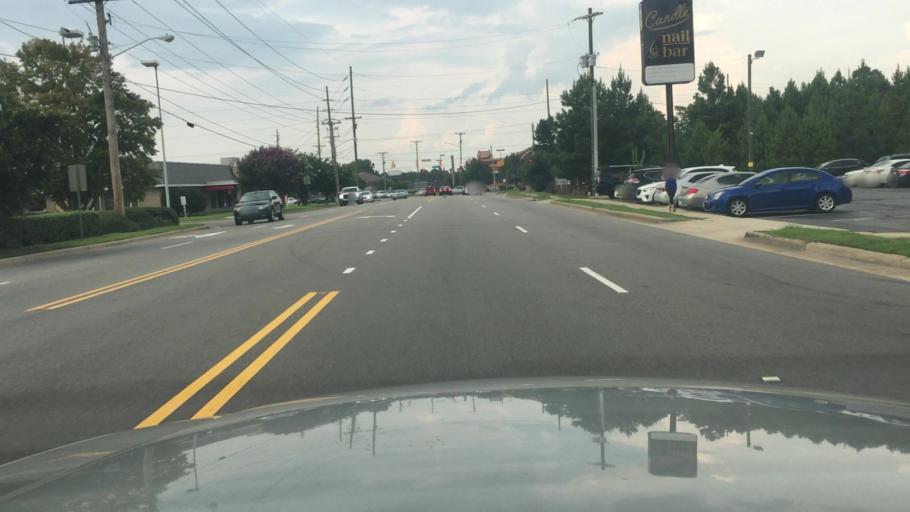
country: US
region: North Carolina
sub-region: Cumberland County
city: Fayetteville
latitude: 35.0655
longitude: -78.9508
